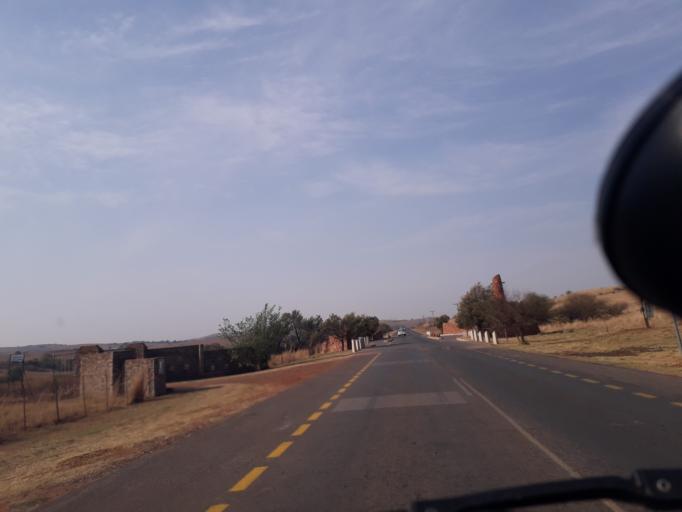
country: ZA
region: Gauteng
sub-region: West Rand District Municipality
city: Krugersdorp
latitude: -26.0222
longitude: 27.7242
